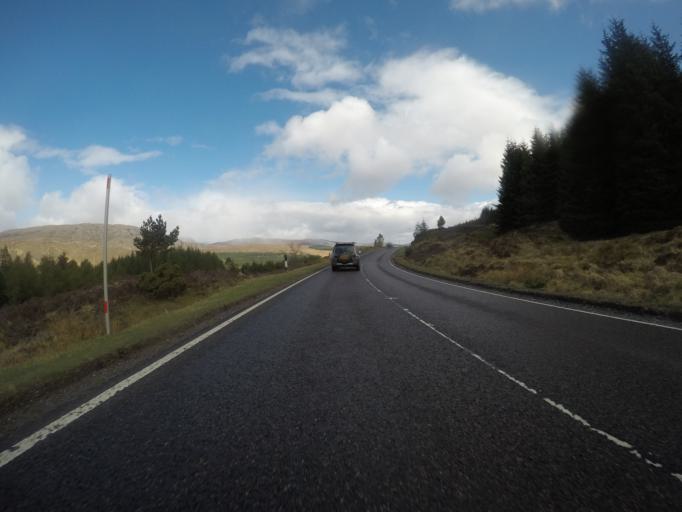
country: GB
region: Scotland
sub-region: Highland
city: Spean Bridge
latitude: 57.1079
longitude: -4.9849
